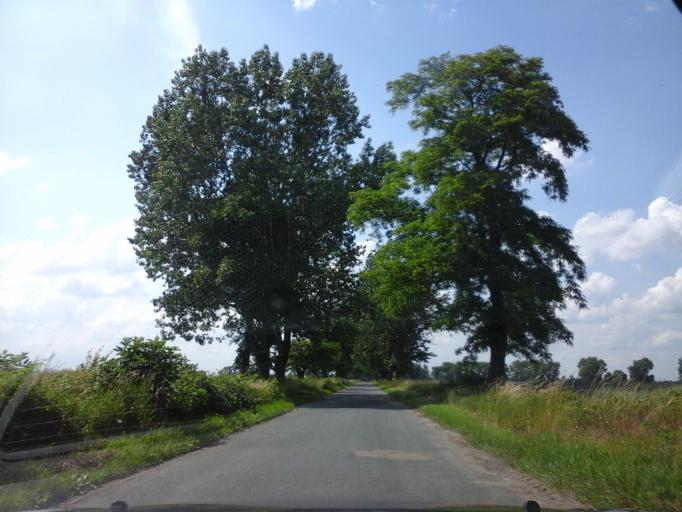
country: PL
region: West Pomeranian Voivodeship
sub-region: Powiat choszczenski
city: Choszczno
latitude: 53.1238
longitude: 15.3948
